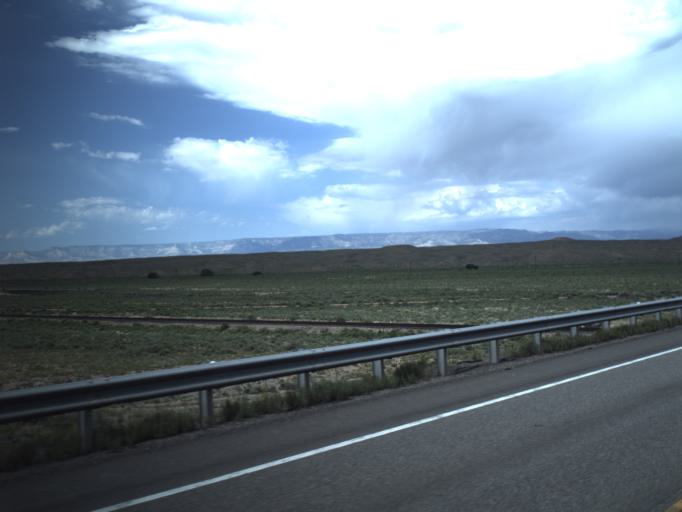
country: US
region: Utah
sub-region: Carbon County
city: East Carbon City
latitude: 39.5213
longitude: -110.5630
